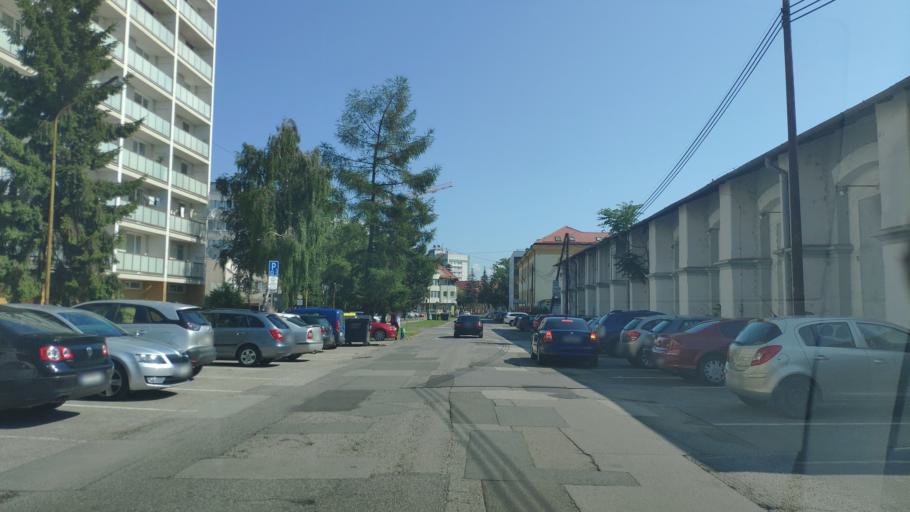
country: SK
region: Kosicky
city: Kosice
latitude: 48.7136
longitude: 21.2488
